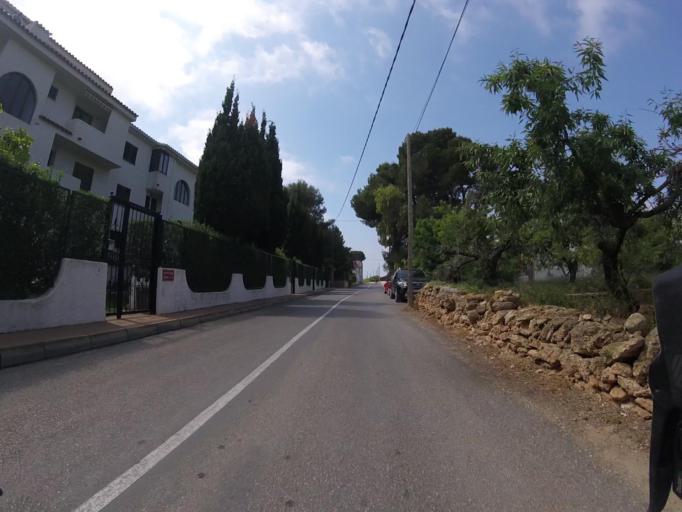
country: ES
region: Valencia
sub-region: Provincia de Castello
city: Alcoceber
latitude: 40.2397
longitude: 0.2681
